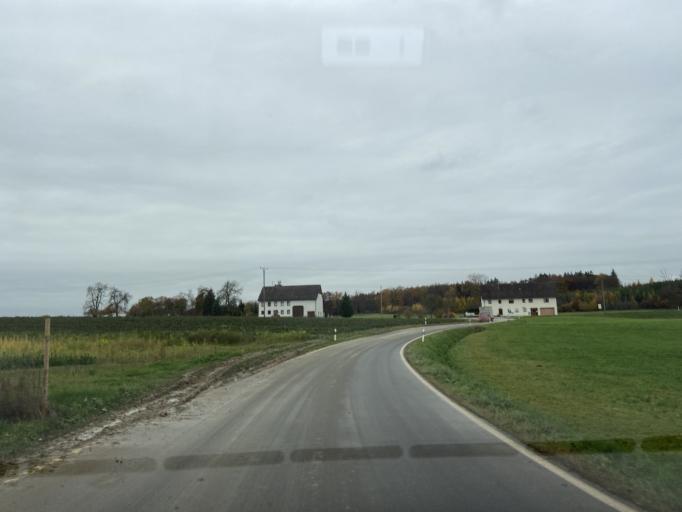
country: DE
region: Baden-Wuerttemberg
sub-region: Tuebingen Region
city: Wald
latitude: 47.9708
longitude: 9.1583
